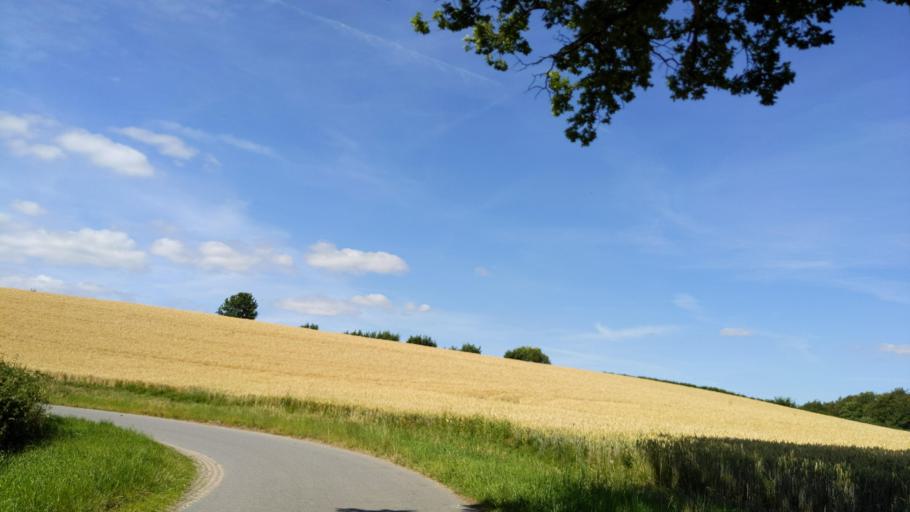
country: DE
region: Schleswig-Holstein
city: Kasseedorf
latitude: 54.1376
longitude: 10.7406
